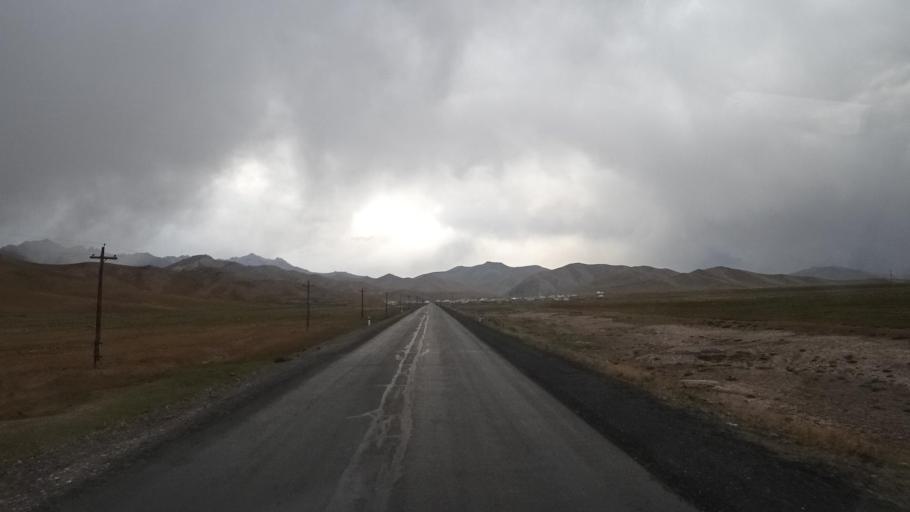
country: KG
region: Osh
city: Gul'cha
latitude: 39.7149
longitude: 73.2393
